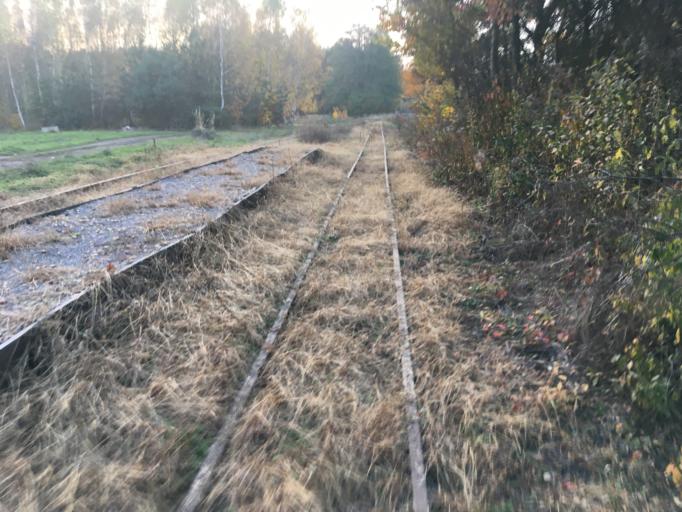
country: PL
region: Swietokrzyskie
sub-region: Powiat starachowicki
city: Starachowice
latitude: 51.0673
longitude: 21.1287
